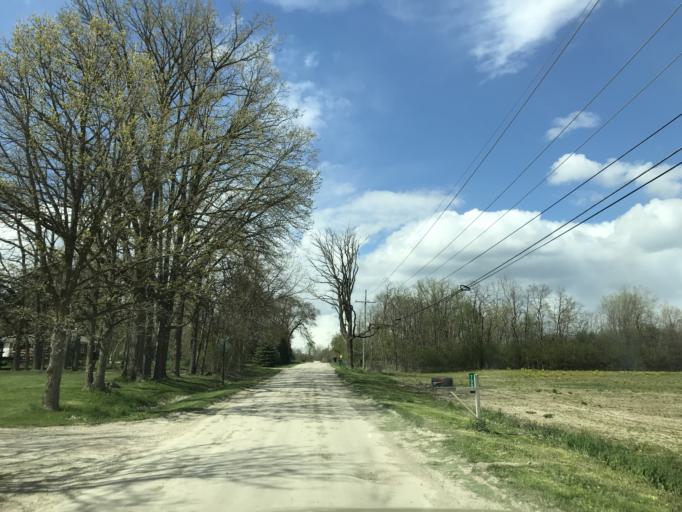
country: US
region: Michigan
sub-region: Oakland County
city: South Lyon
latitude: 42.3827
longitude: -83.6250
